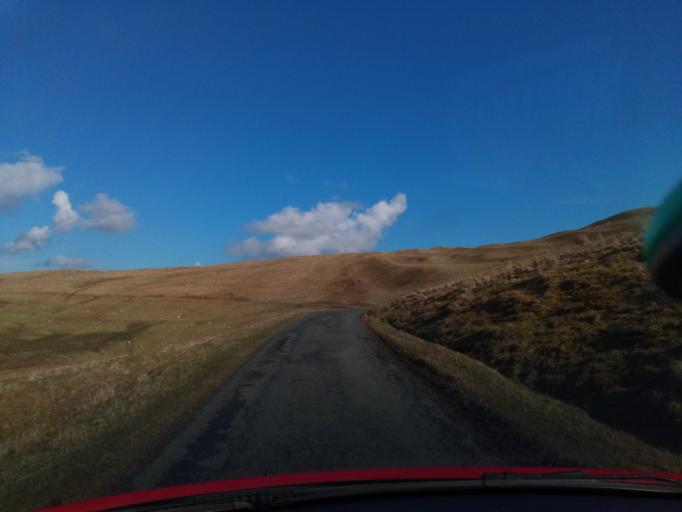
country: GB
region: Scotland
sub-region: The Scottish Borders
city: Hawick
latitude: 55.4530
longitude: -2.8818
